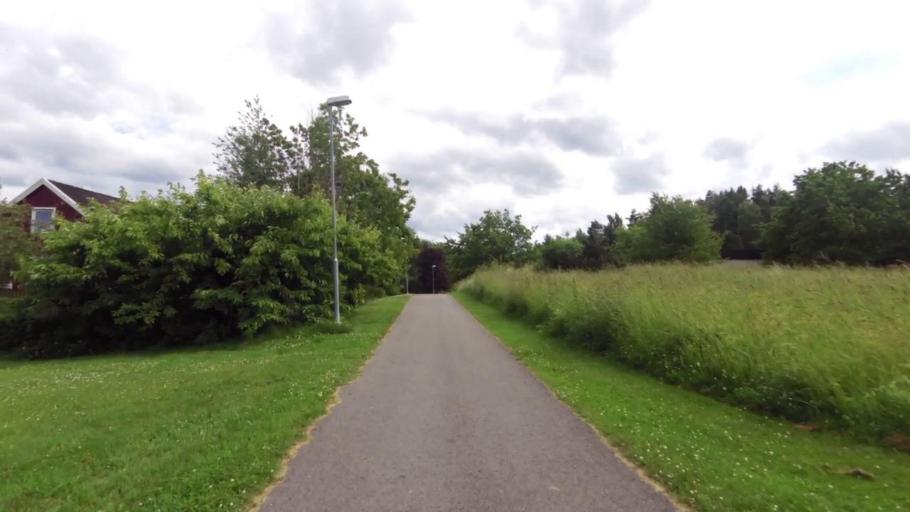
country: SE
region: OEstergoetland
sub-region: Linkopings Kommun
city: Malmslatt
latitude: 58.4167
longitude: 15.5572
